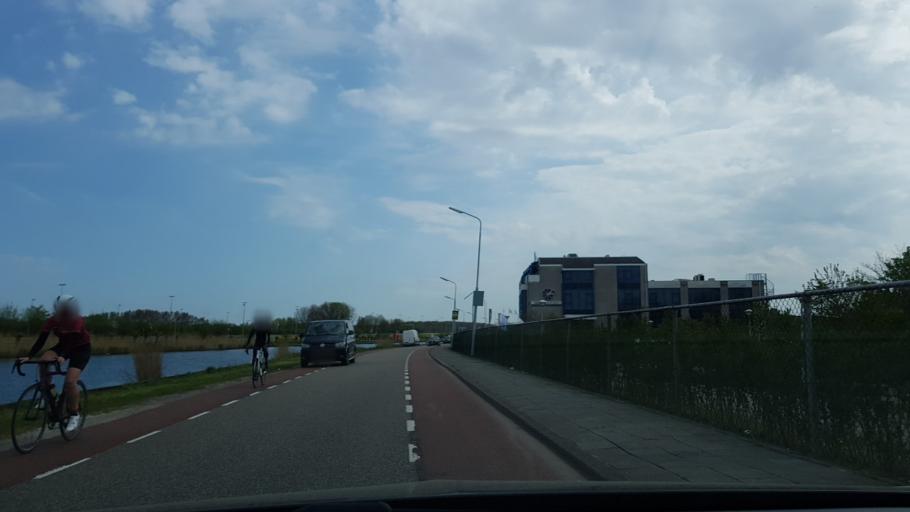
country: NL
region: North Holland
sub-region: Gemeente Haarlem
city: Haarlem
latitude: 52.3858
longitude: 4.7283
